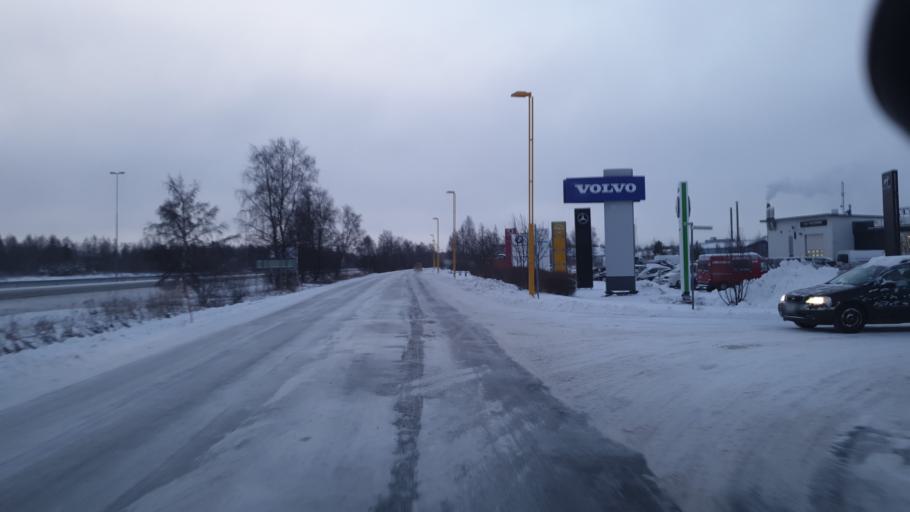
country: FI
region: Lapland
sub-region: Kemi-Tornio
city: Kemi
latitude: 65.7414
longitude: 24.5851
